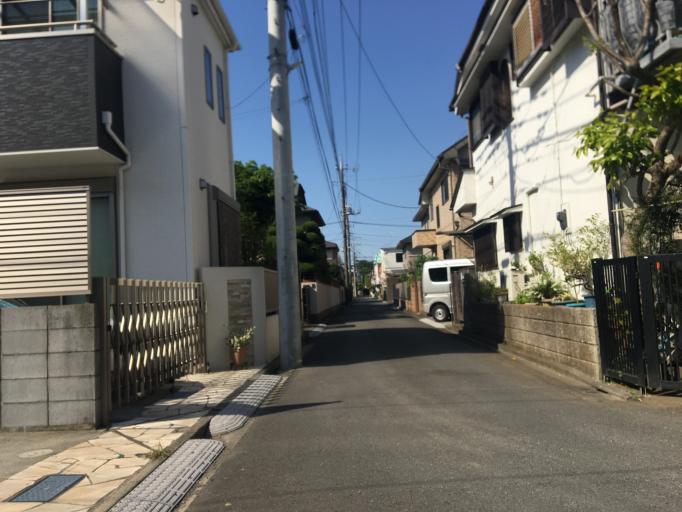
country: JP
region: Tokyo
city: Kokubunji
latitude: 35.7119
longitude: 139.4856
